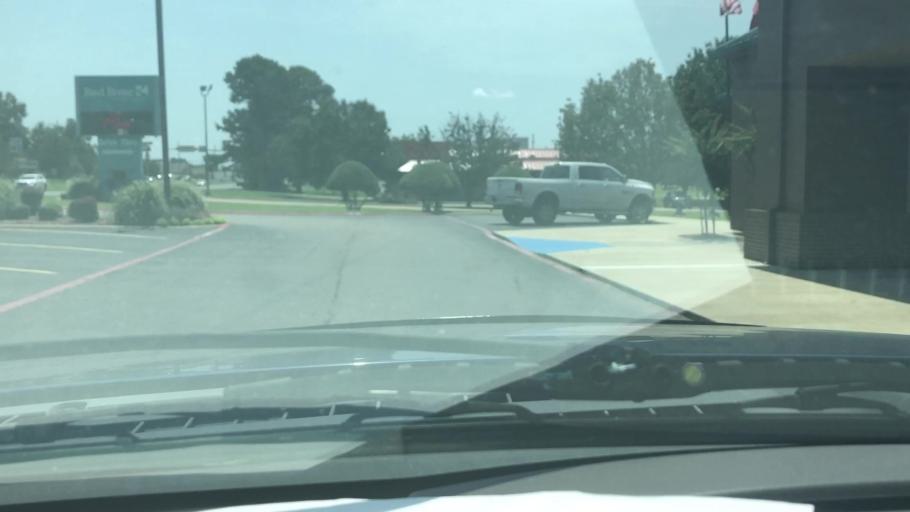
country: US
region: Arkansas
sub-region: Miller County
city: Texarkana
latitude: 33.4593
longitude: -94.0660
